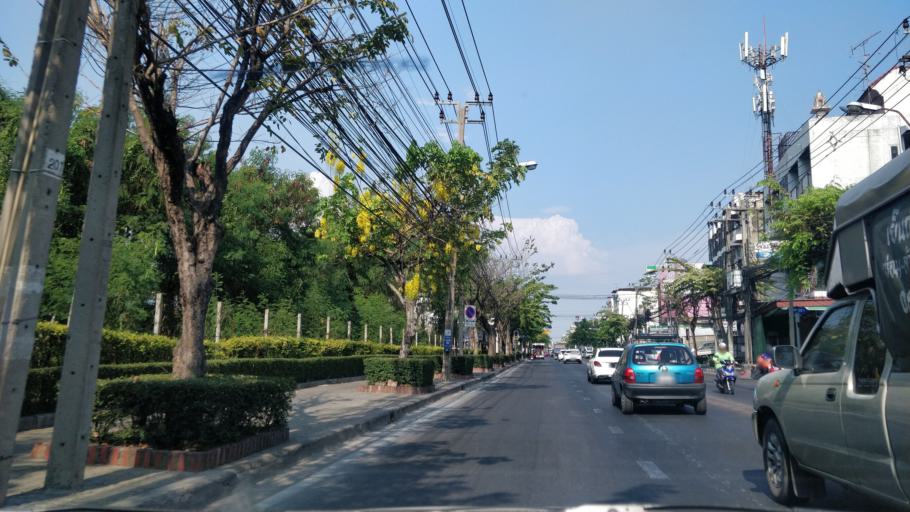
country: TH
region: Bangkok
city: Phra Khanong
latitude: 13.7097
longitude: 100.6250
